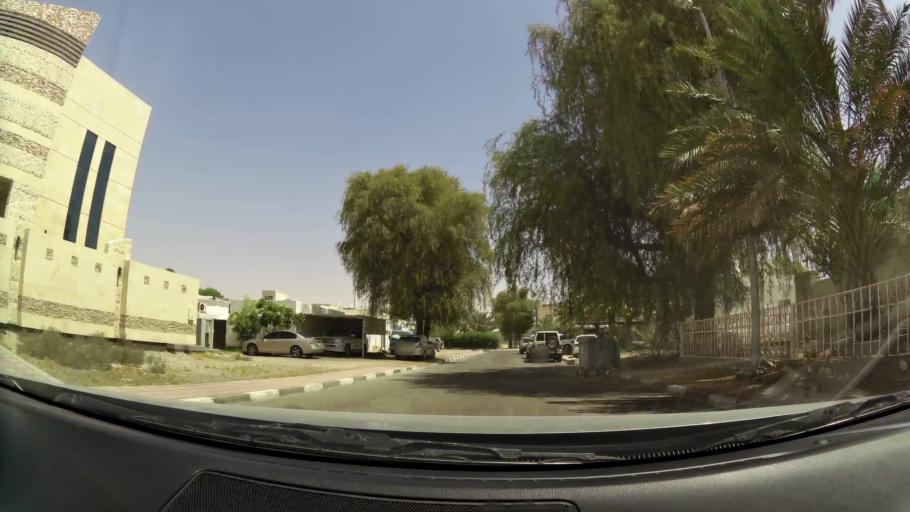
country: OM
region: Al Buraimi
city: Al Buraymi
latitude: 24.2754
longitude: 55.7679
